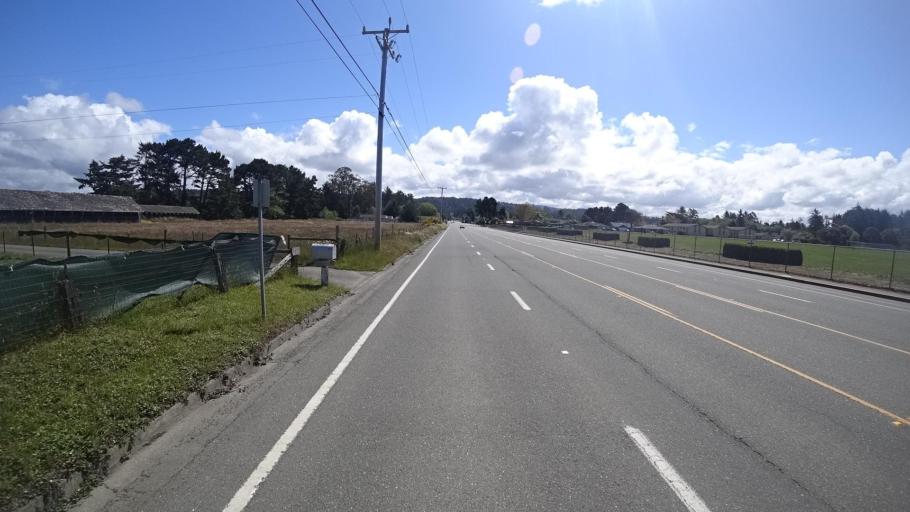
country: US
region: California
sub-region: Humboldt County
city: McKinleyville
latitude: 40.9563
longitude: -124.1077
